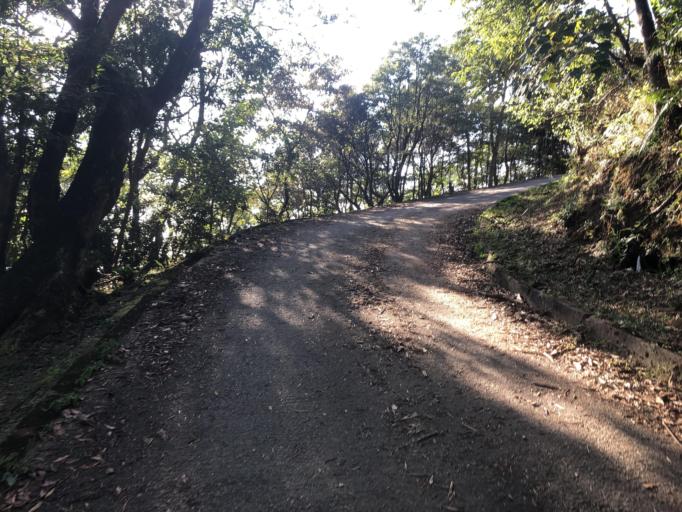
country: HK
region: Tsuen Wan
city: Tsuen Wan
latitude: 22.3972
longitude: 114.0889
